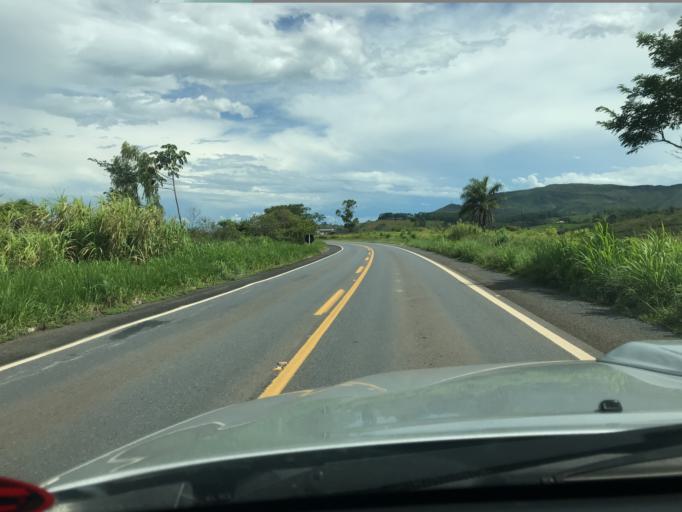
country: BR
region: Minas Gerais
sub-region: Campos Altos
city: Campos Altos
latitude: -19.8021
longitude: -46.0344
